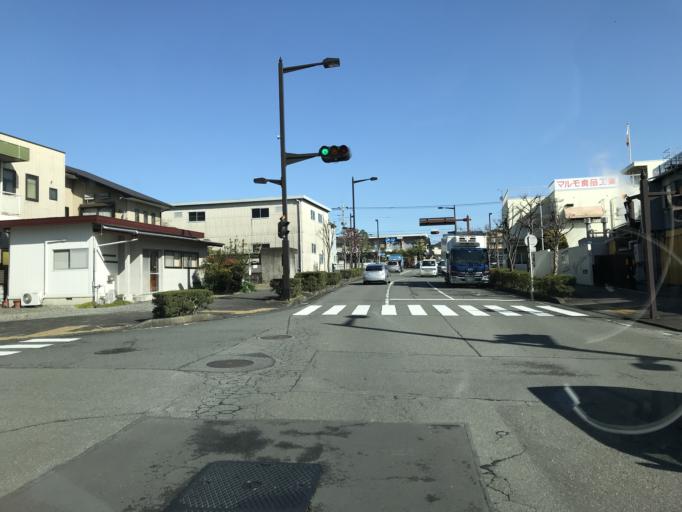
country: JP
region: Shizuoka
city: Fujinomiya
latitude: 35.2227
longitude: 138.6224
